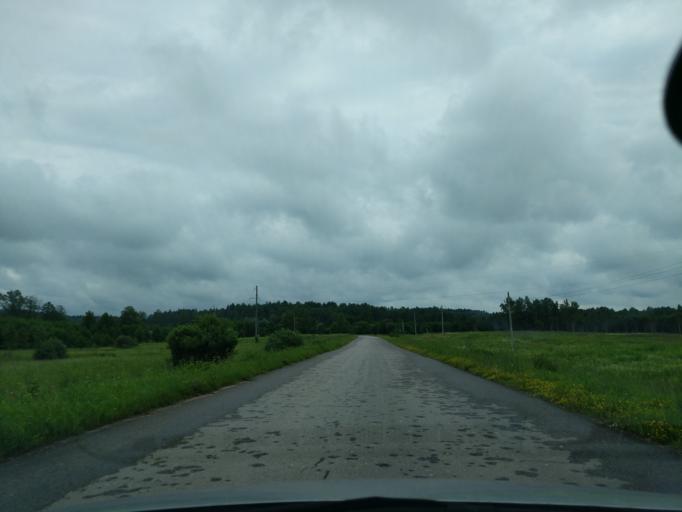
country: RU
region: Kaluga
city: Myatlevo
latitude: 54.8138
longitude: 35.6776
